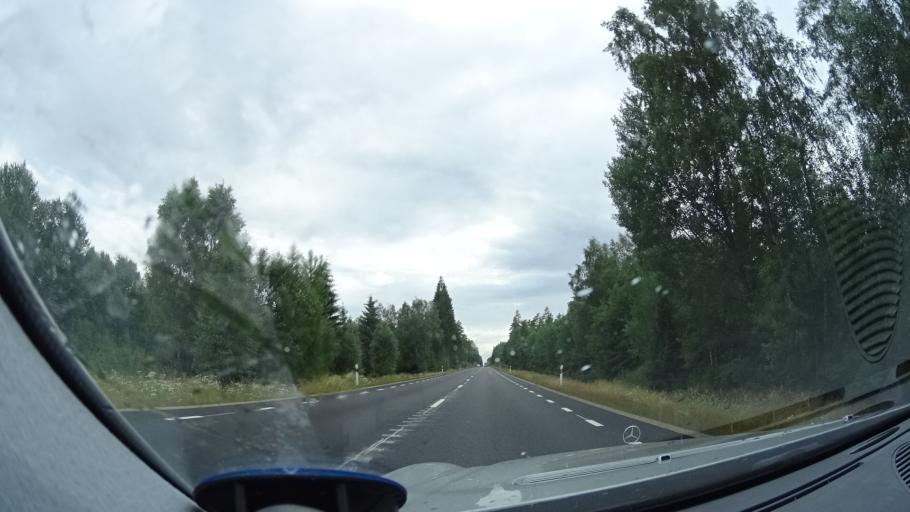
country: SE
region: Kronoberg
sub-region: Tingsryds Kommun
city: Tingsryd
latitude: 56.4127
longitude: 14.9439
